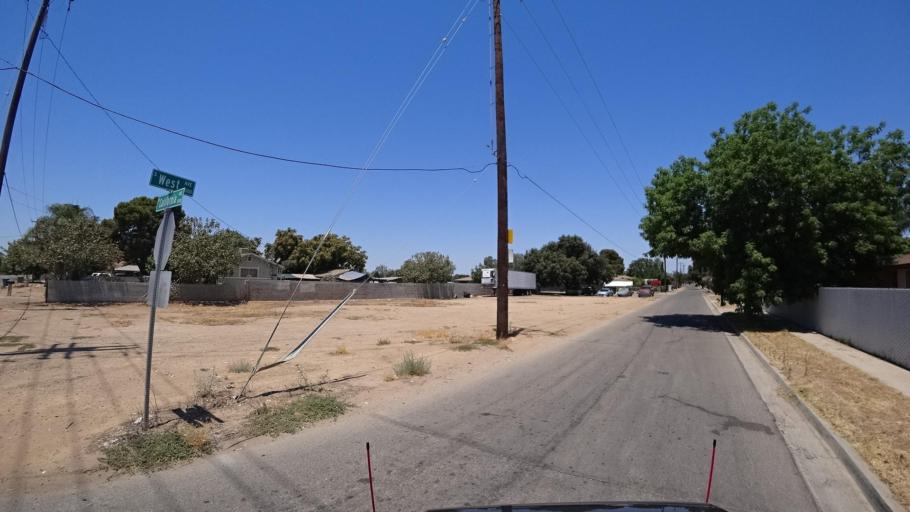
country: US
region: California
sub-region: Fresno County
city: West Park
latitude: 36.7214
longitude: -119.8267
